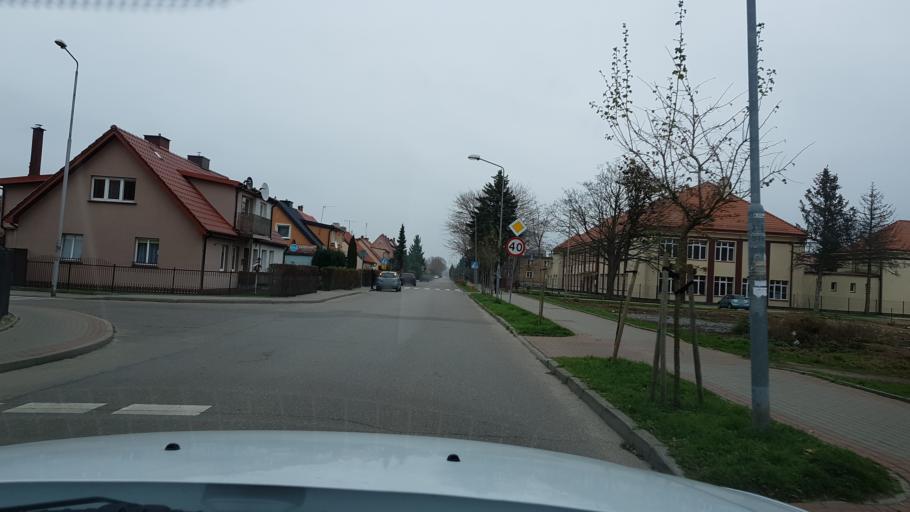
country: PL
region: West Pomeranian Voivodeship
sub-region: Powiat slawienski
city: Darlowo
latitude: 54.4197
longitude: 16.4167
